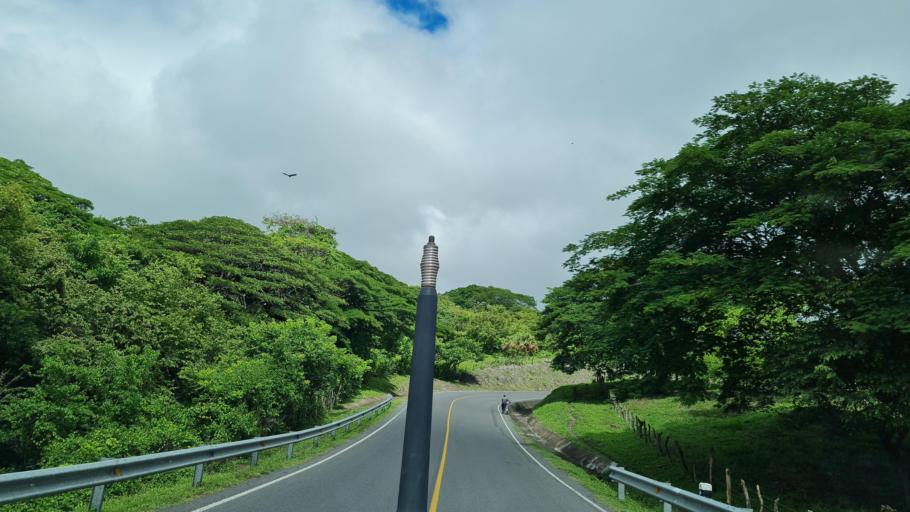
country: NI
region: Matagalpa
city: Terrabona
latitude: 12.5904
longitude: -85.9143
